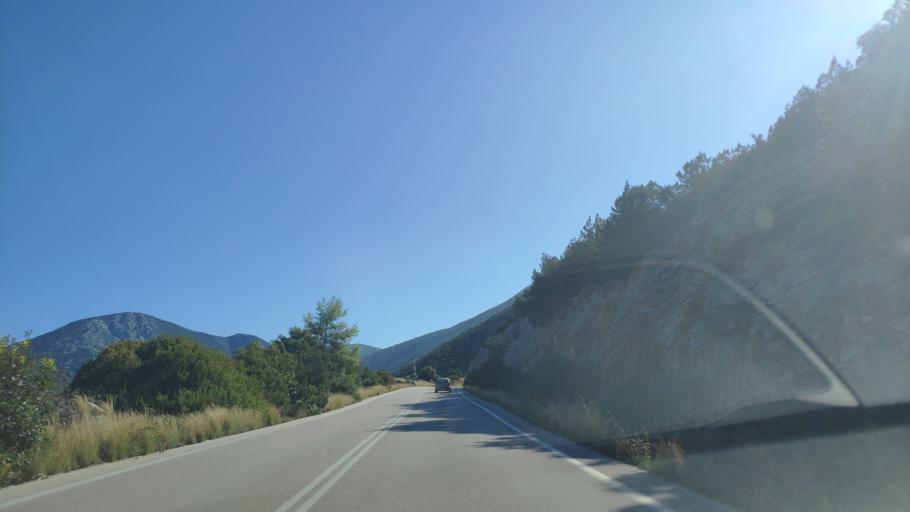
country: GR
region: Peloponnese
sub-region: Nomos Argolidos
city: Palaia Epidavros
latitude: 37.6230
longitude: 23.1464
